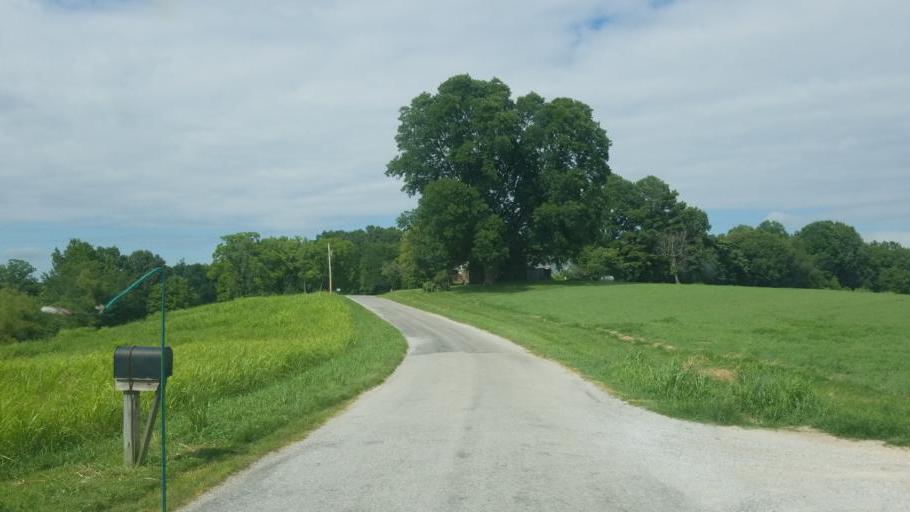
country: US
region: Illinois
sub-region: Union County
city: Cobden
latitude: 37.6061
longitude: -89.3629
